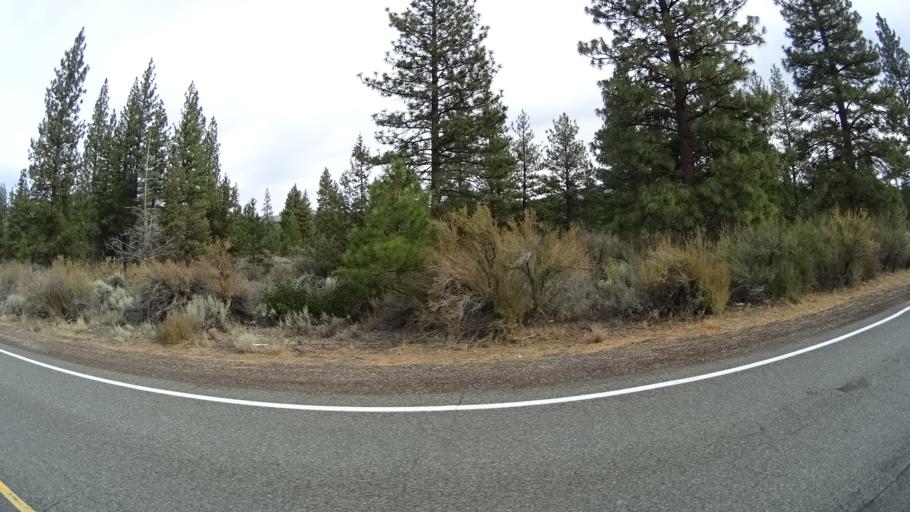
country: US
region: California
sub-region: Siskiyou County
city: Weed
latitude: 41.5450
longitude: -122.2471
